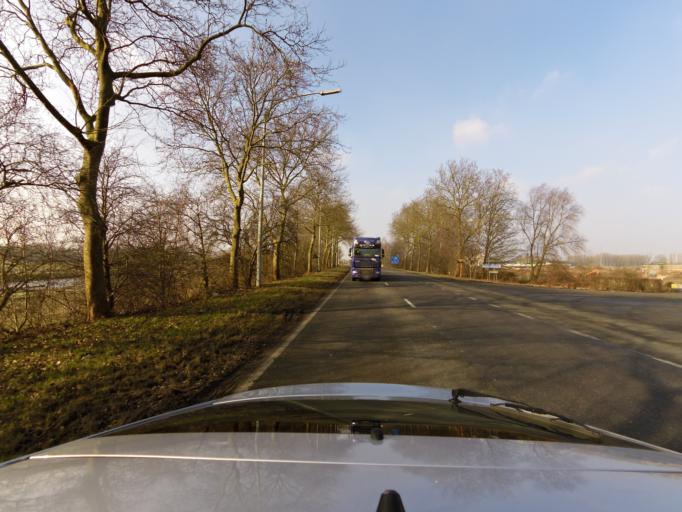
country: BE
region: Wallonia
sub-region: Province du Hainaut
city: Boussu
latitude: 50.4780
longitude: 3.7816
